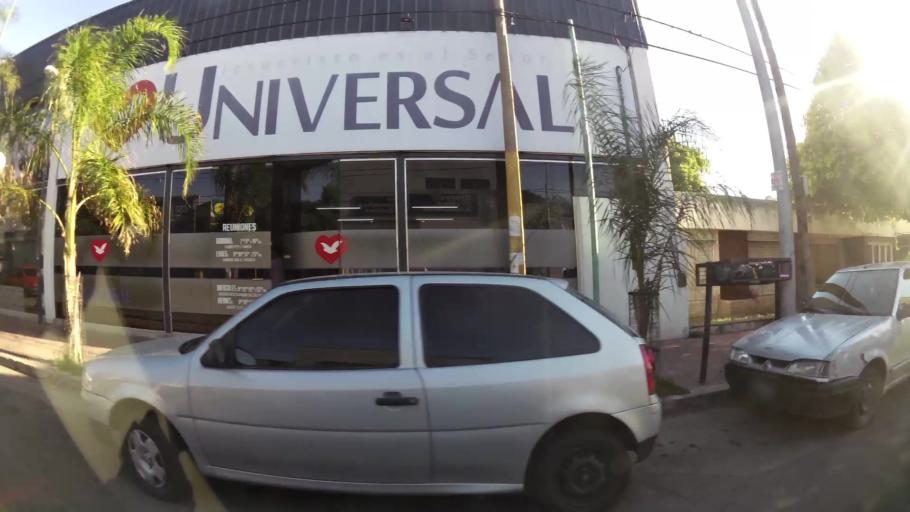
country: AR
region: Cordoba
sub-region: Departamento de Capital
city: Cordoba
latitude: -31.3806
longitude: -64.1833
